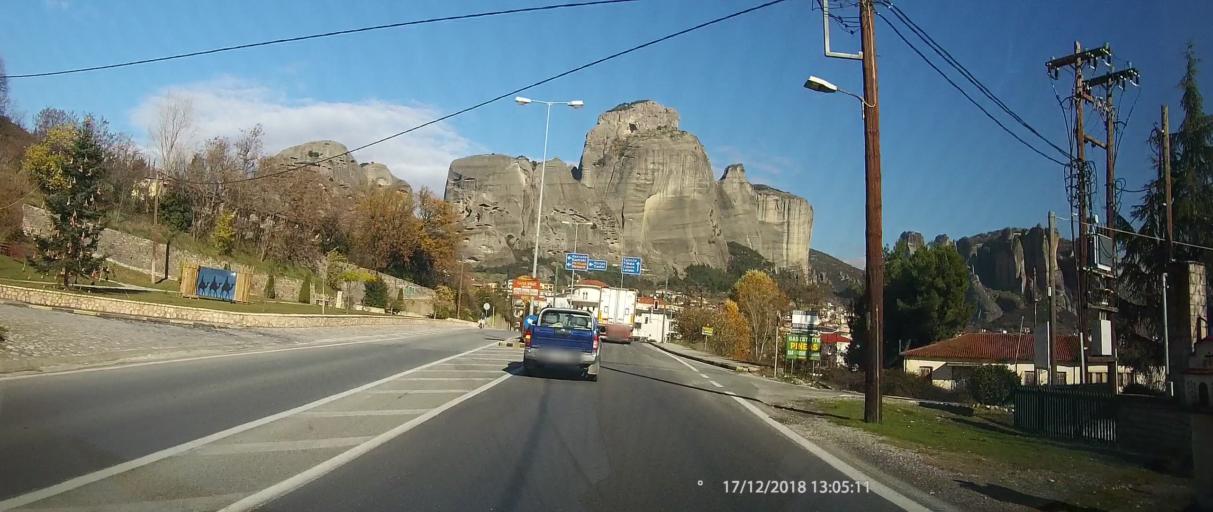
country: GR
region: Thessaly
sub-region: Trikala
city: Kalampaka
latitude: 39.7031
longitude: 21.6168
